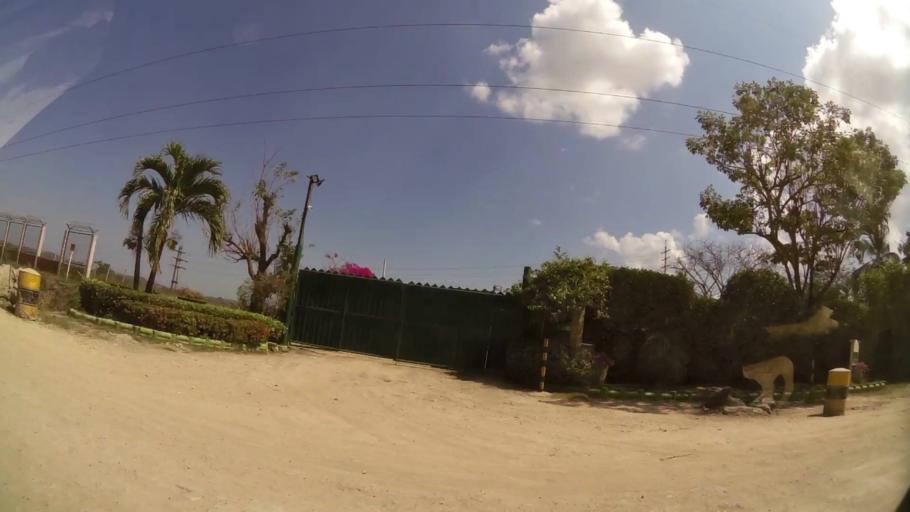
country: CO
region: Bolivar
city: Cartagena
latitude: 10.3465
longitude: -75.4872
